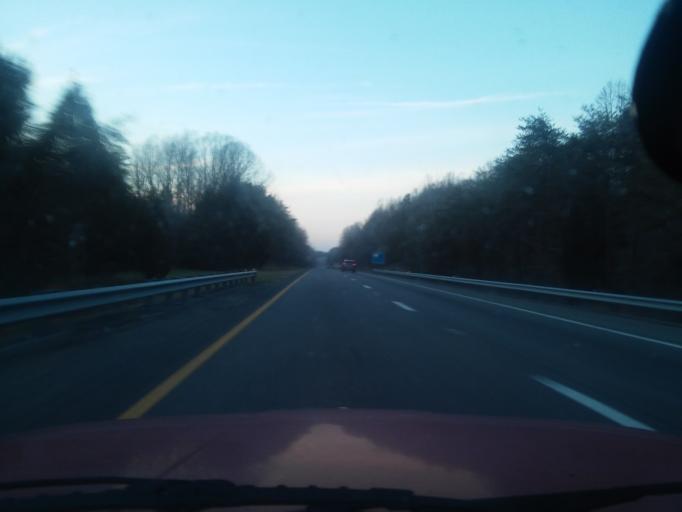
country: US
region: Virginia
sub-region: Goochland County
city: Goochland
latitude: 37.8329
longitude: -77.9683
